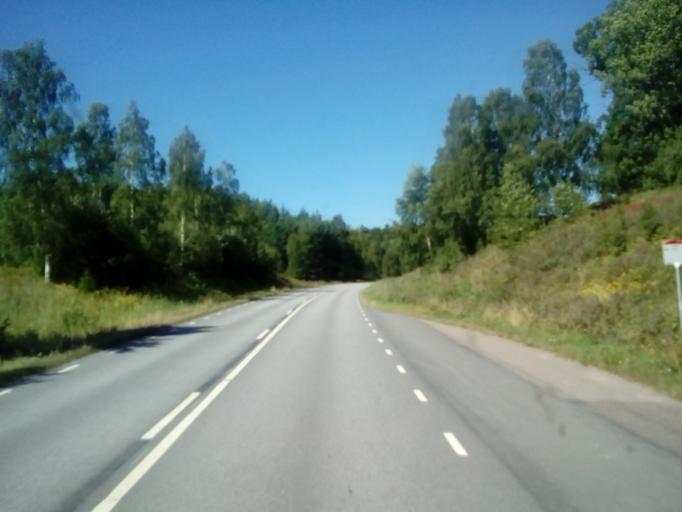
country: SE
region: Kalmar
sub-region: Vimmerby Kommun
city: Sodra Vi
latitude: 57.9134
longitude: 15.9606
